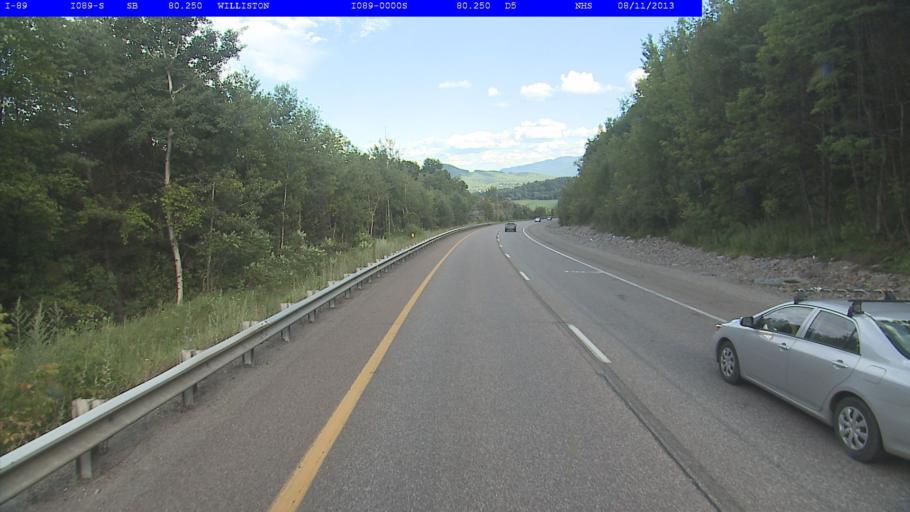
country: US
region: Vermont
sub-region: Chittenden County
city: Williston
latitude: 44.4321
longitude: -73.0412
